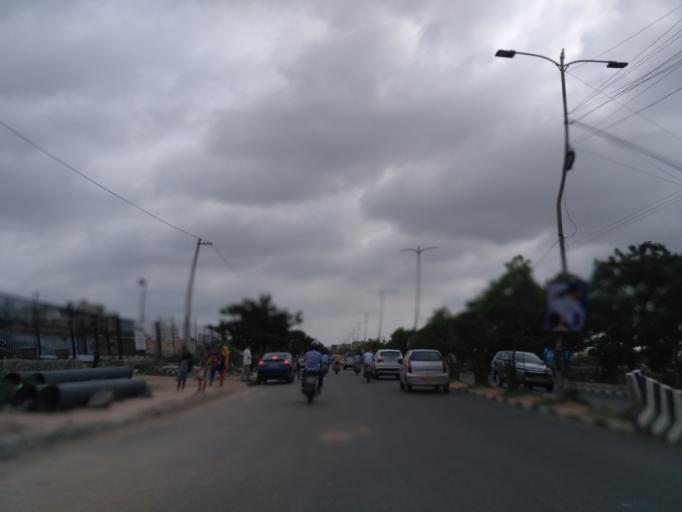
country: IN
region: Telangana
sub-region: Rangareddi
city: Kukatpalli
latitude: 17.4472
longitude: 78.3950
